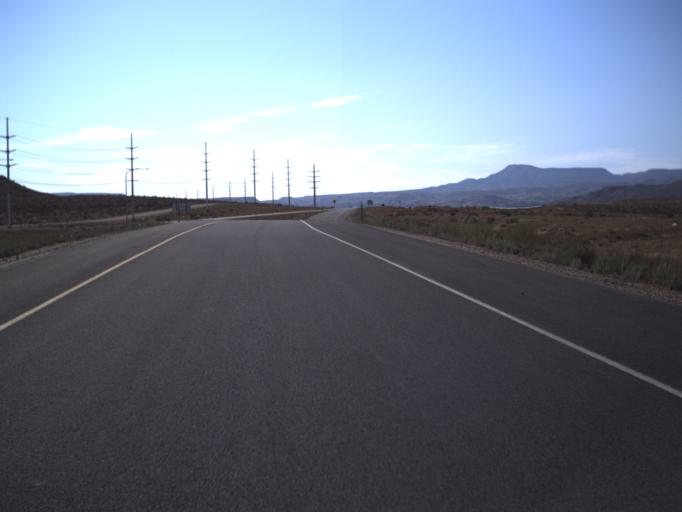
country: US
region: Utah
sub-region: Washington County
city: Washington
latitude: 37.0580
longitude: -113.4865
